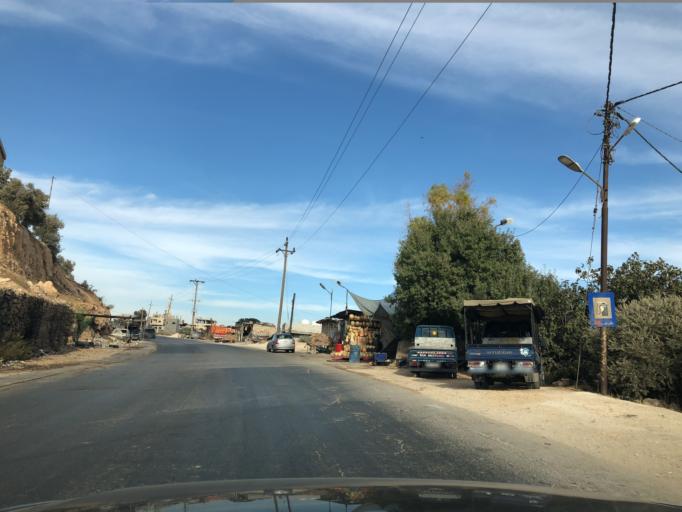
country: JO
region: Irbid
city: Raymun
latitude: 32.2849
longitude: 35.8258
